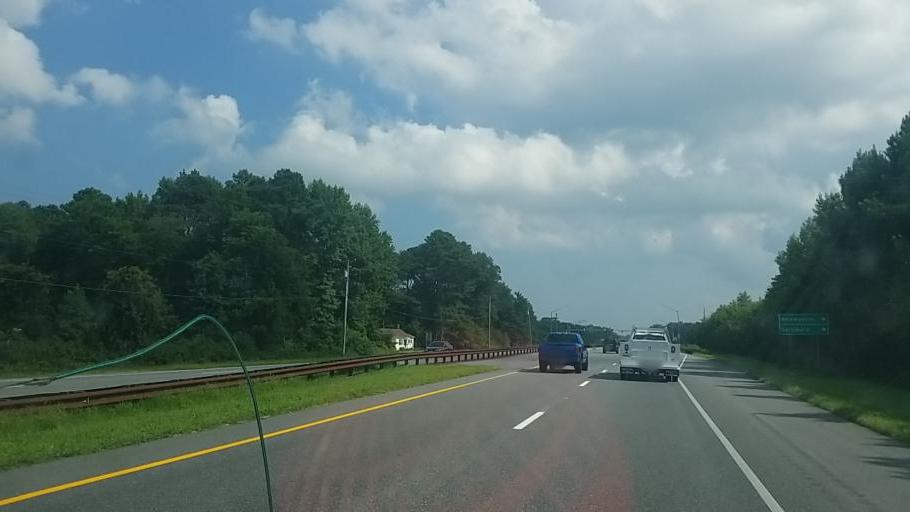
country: US
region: Delaware
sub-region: Sussex County
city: Selbyville
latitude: 38.4432
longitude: -75.2279
